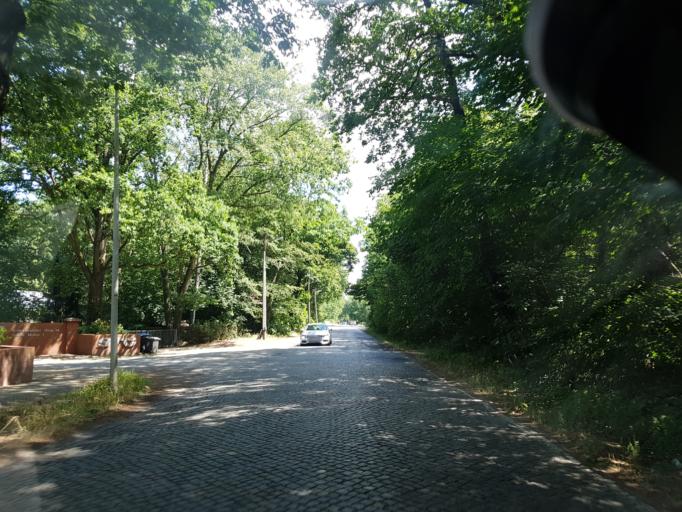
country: DE
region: Brandenburg
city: Cottbus
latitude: 51.7202
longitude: 14.3543
